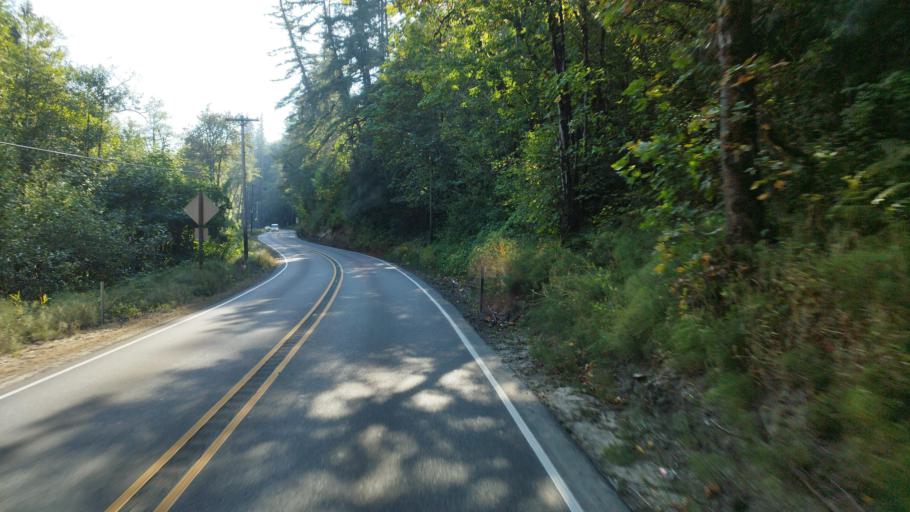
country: US
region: Oregon
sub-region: Washington County
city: Bethany
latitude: 45.6453
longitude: -122.8580
